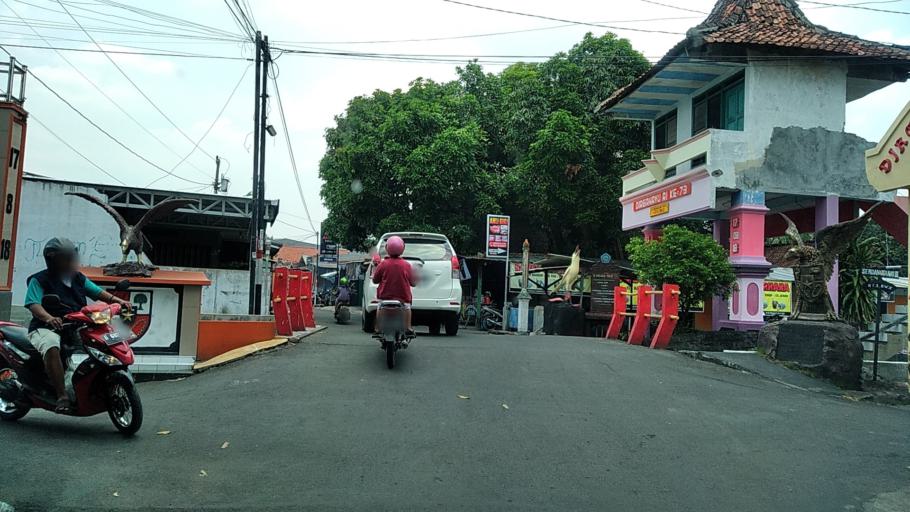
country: ID
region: Central Java
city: Semarang
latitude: -7.0072
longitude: 110.4553
